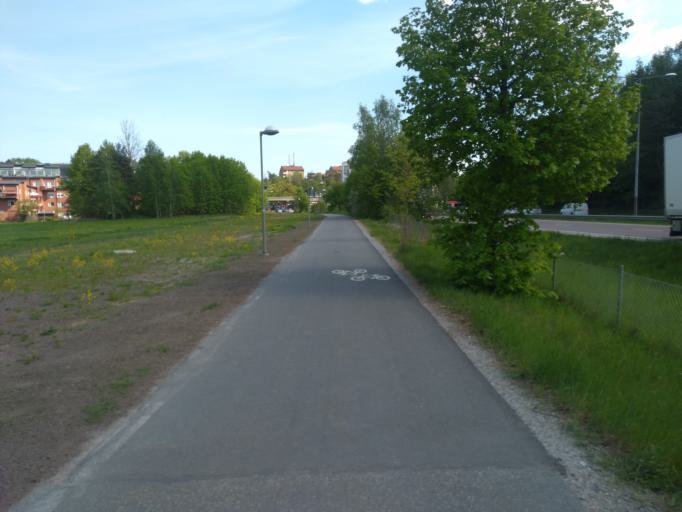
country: SE
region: Stockholm
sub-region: Stockholms Kommun
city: Arsta
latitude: 59.2587
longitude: 18.0775
